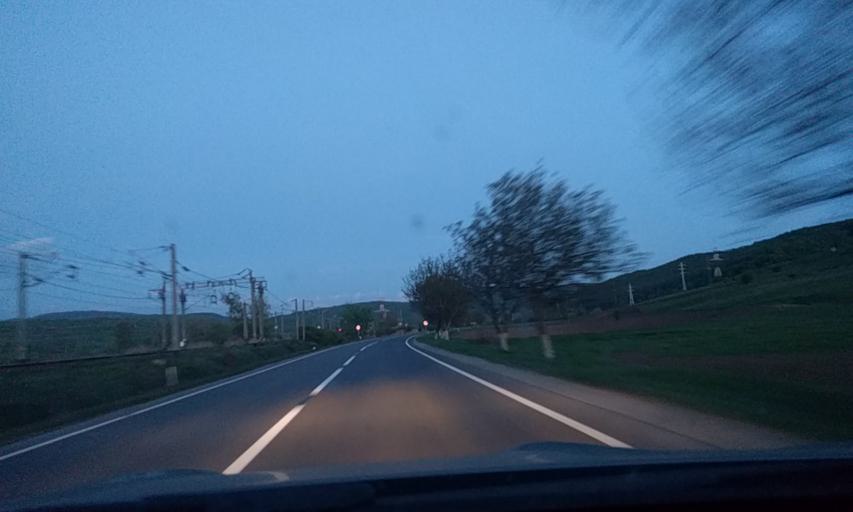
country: RO
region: Mures
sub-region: Comuna Vanatori
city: Vanatori
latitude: 46.2412
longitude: 24.9590
